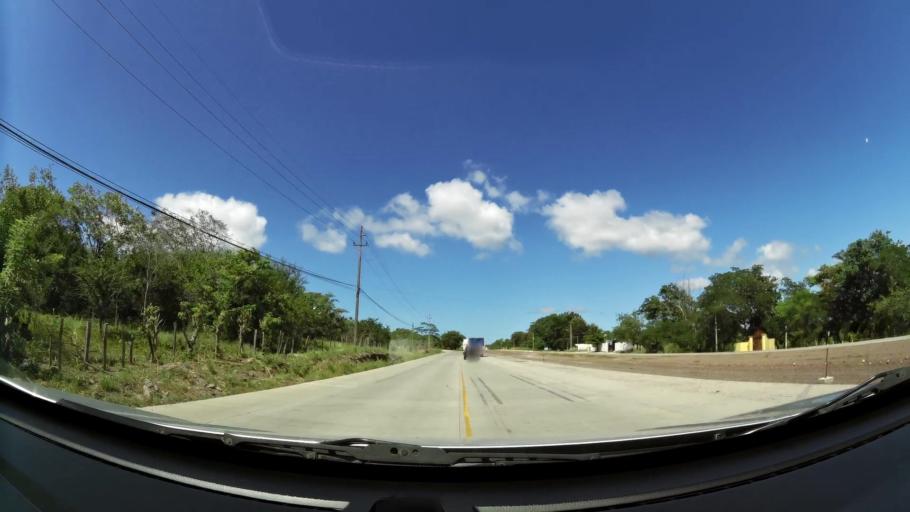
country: CR
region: Guanacaste
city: Bagaces
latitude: 10.5072
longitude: -85.2341
